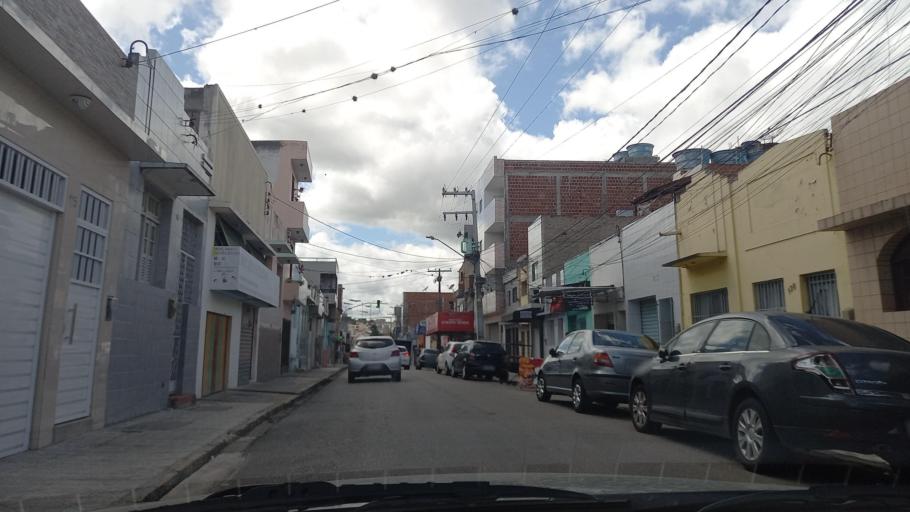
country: BR
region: Pernambuco
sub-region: Caruaru
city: Caruaru
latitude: -8.2850
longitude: -35.9657
